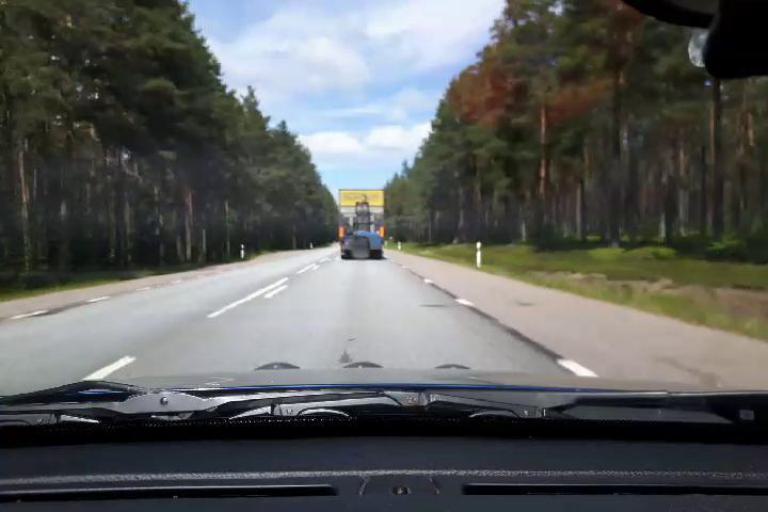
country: SE
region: Uppsala
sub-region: Tierps Kommun
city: Tierp
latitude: 60.1901
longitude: 17.4785
